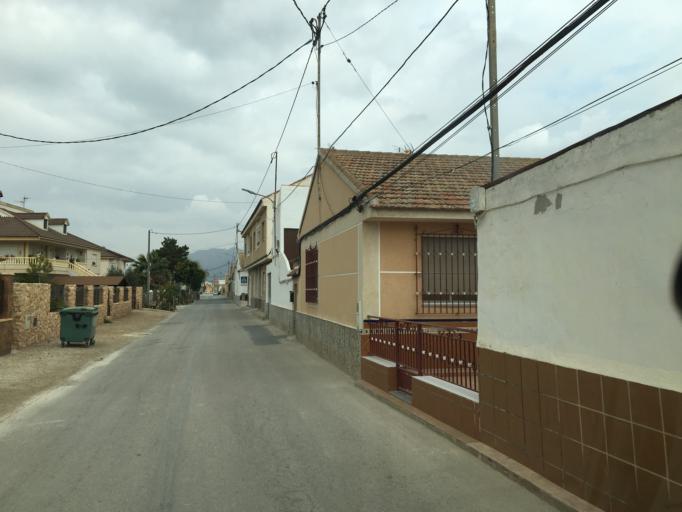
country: ES
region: Murcia
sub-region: Murcia
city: Beniel
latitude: 38.0352
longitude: -0.9854
